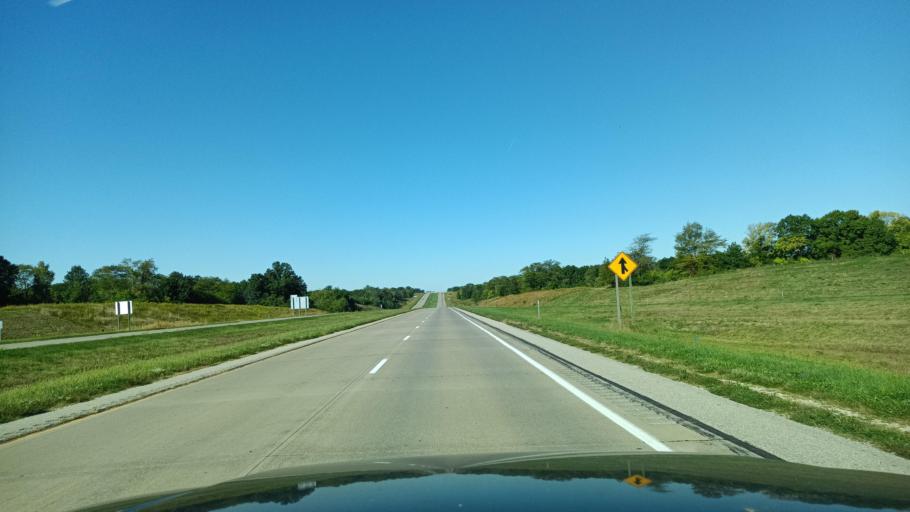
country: US
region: Iowa
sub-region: Lee County
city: Fort Madison
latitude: 40.6708
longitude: -91.2752
